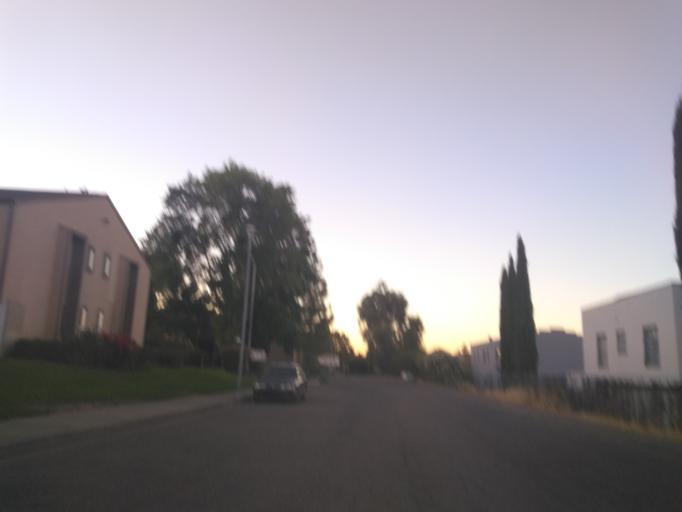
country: US
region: California
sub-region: Mendocino County
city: Ukiah
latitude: 39.1362
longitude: -123.2064
